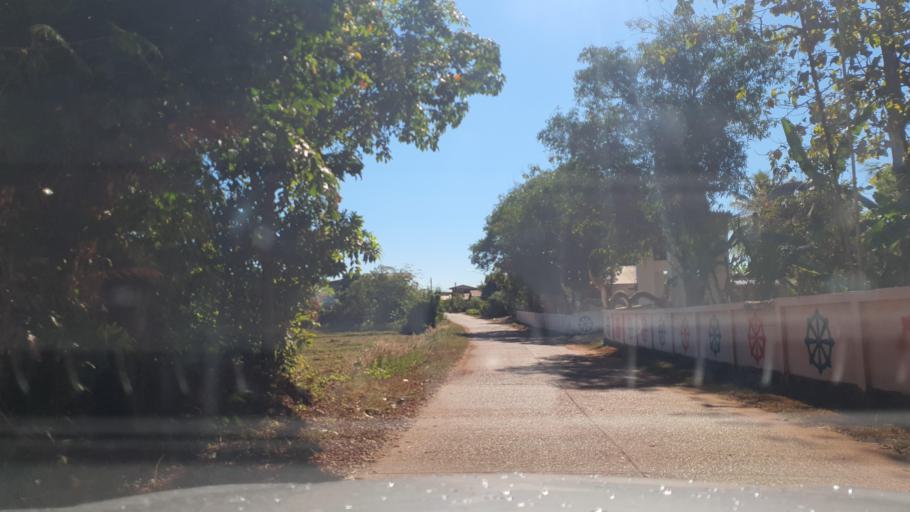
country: TH
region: Nakhon Phanom
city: Ban Phaeng
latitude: 17.8299
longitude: 104.2650
